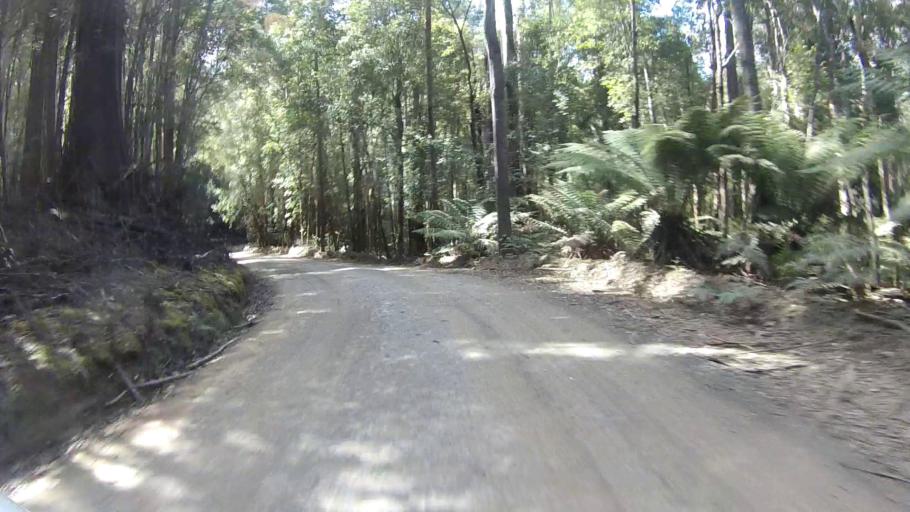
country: AU
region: Tasmania
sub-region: Derwent Valley
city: New Norfolk
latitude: -42.6806
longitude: 146.7014
